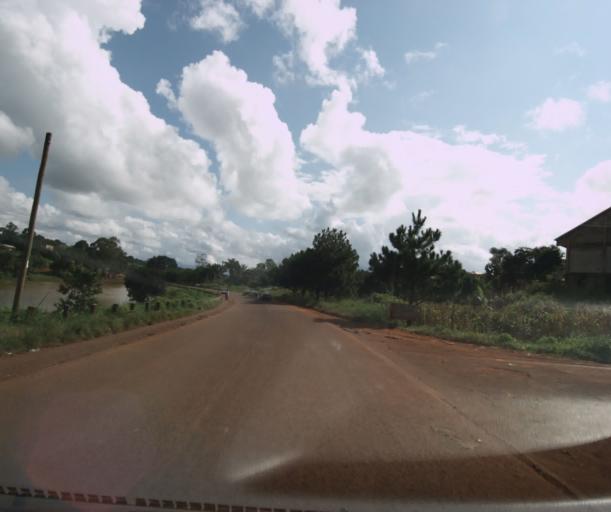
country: CM
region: West
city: Foumban
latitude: 5.7275
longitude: 10.8692
